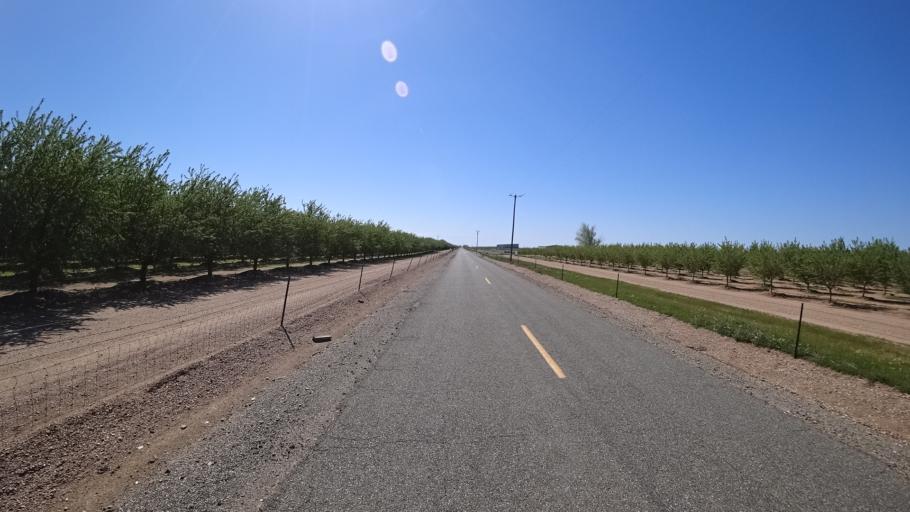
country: US
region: California
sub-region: Glenn County
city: Orland
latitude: 39.6625
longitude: -122.2532
